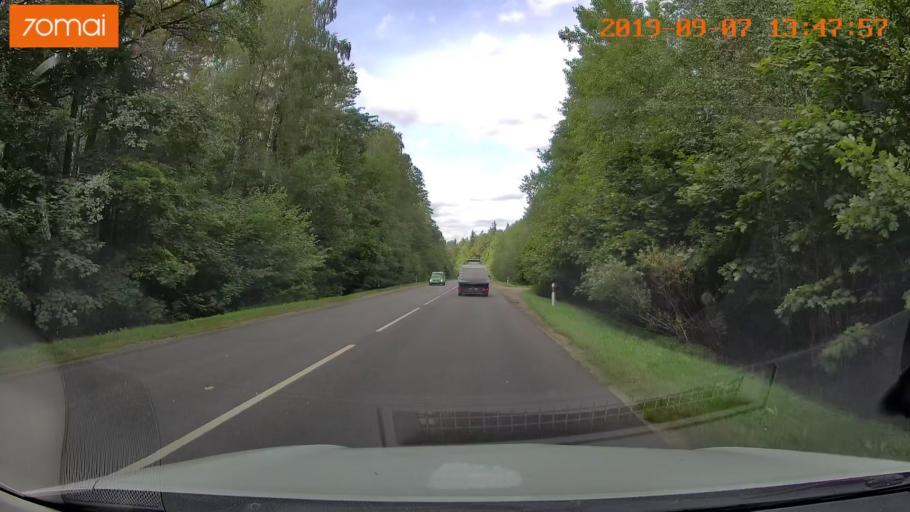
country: LT
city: Baltoji Voke
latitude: 54.6000
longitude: 25.2082
